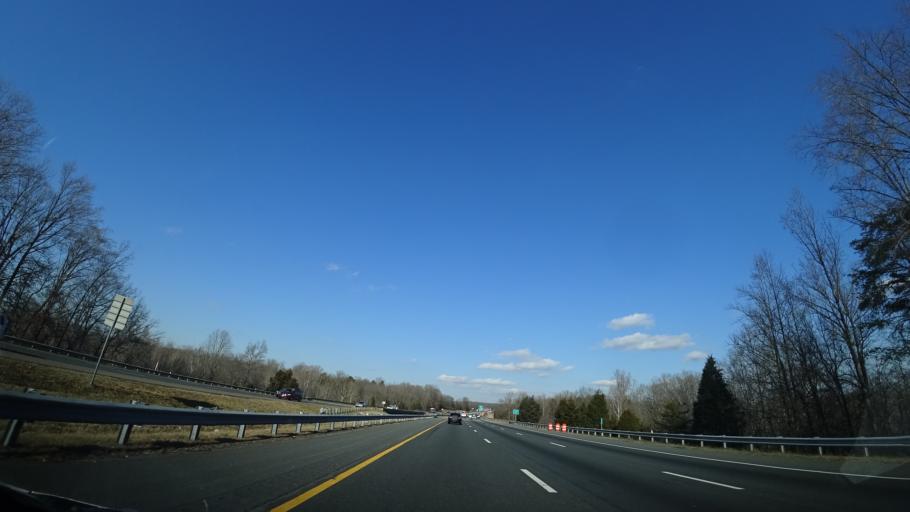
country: US
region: Virginia
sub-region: Spotsylvania County
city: Spotsylvania Courthouse
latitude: 38.1135
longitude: -77.5178
